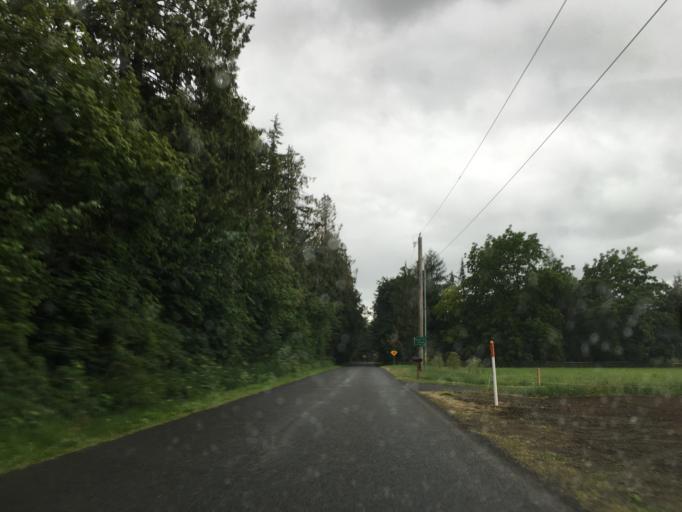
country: US
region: Washington
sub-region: Whatcom County
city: Lynden
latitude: 48.9793
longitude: -122.4596
